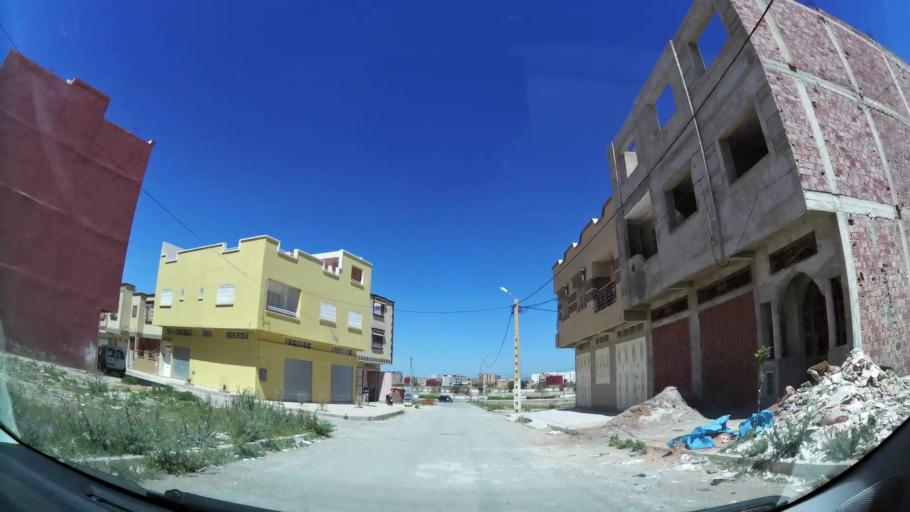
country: MA
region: Oriental
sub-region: Oujda-Angad
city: Oujda
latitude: 34.6708
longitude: -1.8665
